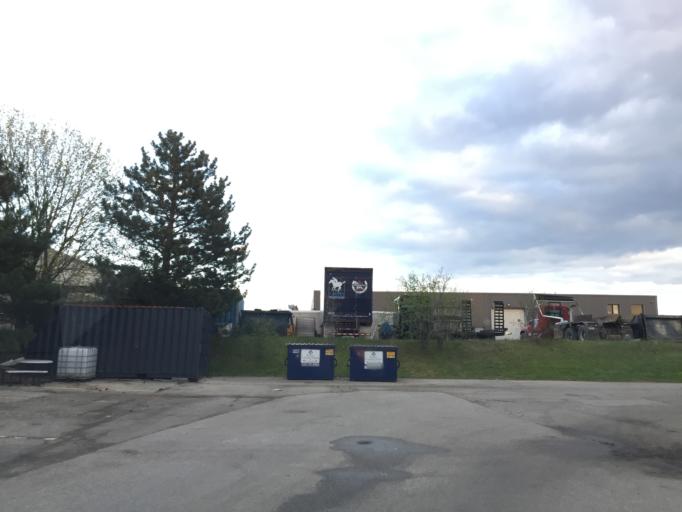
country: CA
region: Ontario
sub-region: Wellington County
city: Guelph
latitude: 43.5344
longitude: -80.3041
